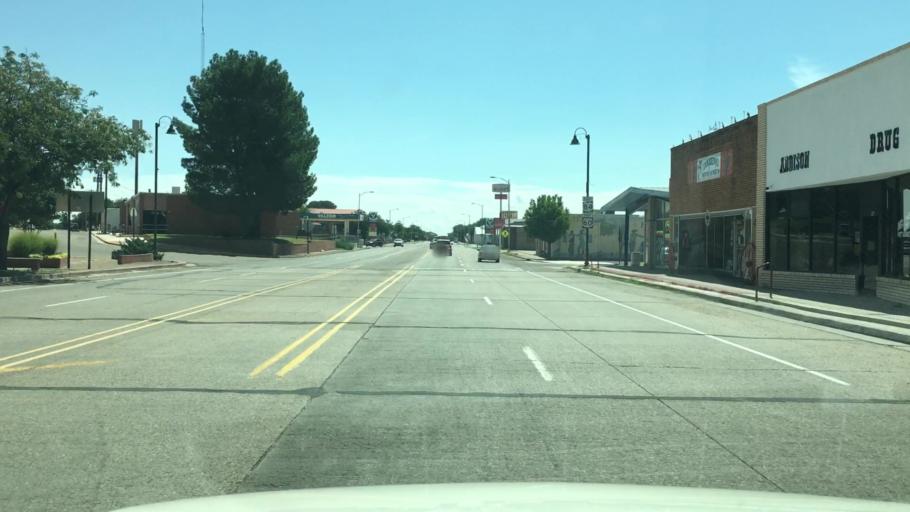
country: US
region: New Mexico
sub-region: De Baca County
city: Fort Sumner
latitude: 34.4717
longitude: -104.2453
